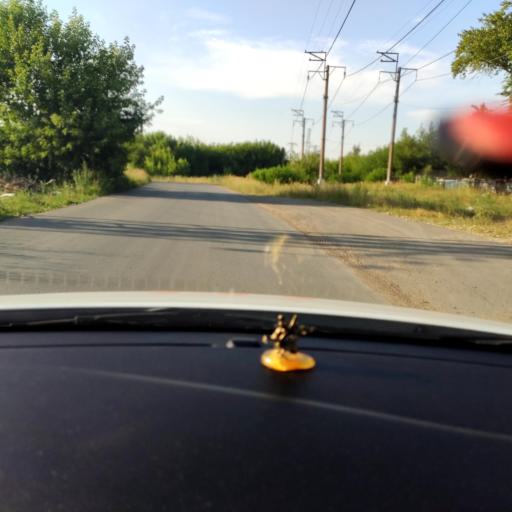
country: RU
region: Tatarstan
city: Staroye Arakchino
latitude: 55.8136
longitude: 48.9116
